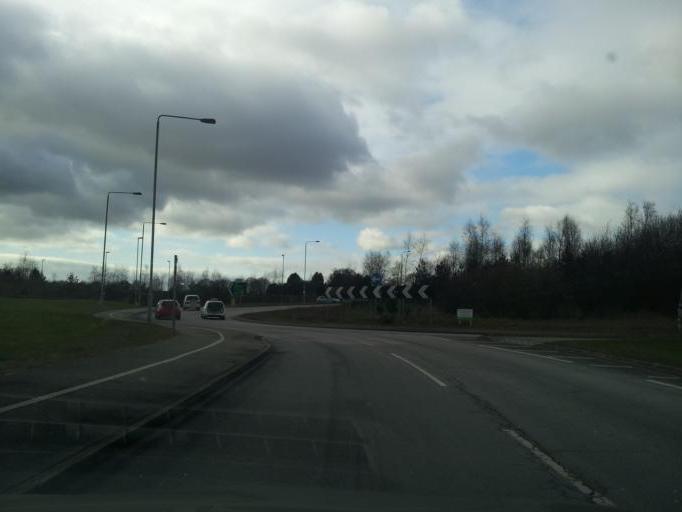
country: GB
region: England
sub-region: Nottinghamshire
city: Rainworth
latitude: 53.1251
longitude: -1.1414
